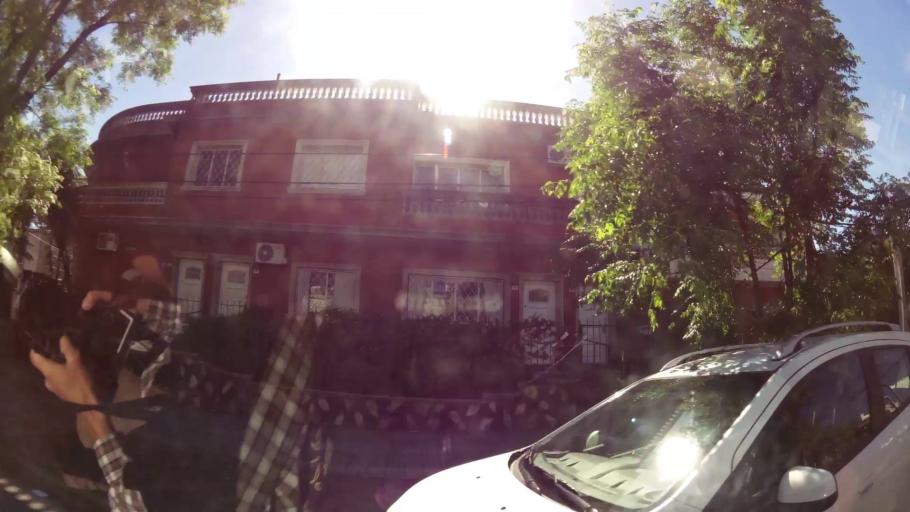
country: UY
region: Montevideo
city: Montevideo
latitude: -34.9001
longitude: -56.1541
